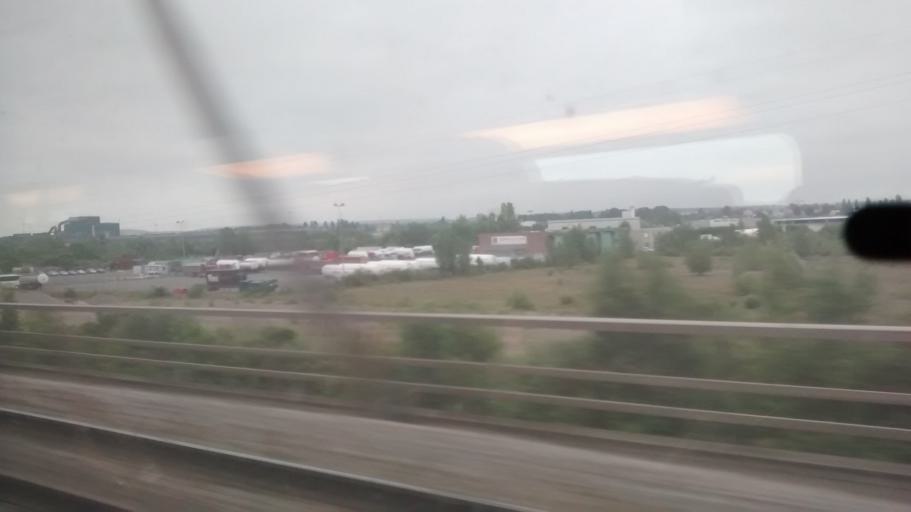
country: FR
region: Ile-de-France
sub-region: Departement de Seine-et-Marne
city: Saint-Germain-Laval
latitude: 48.3967
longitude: 2.9782
